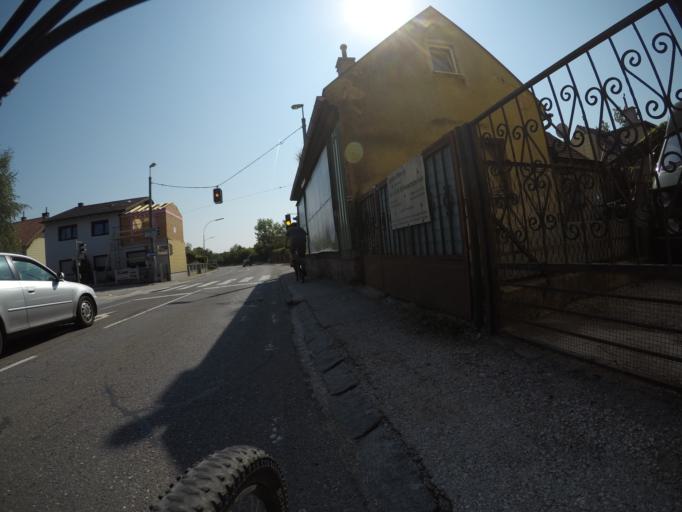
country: AT
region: Lower Austria
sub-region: Politischer Bezirk Baden
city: Hirtenberg
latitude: 47.9364
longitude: 16.1512
